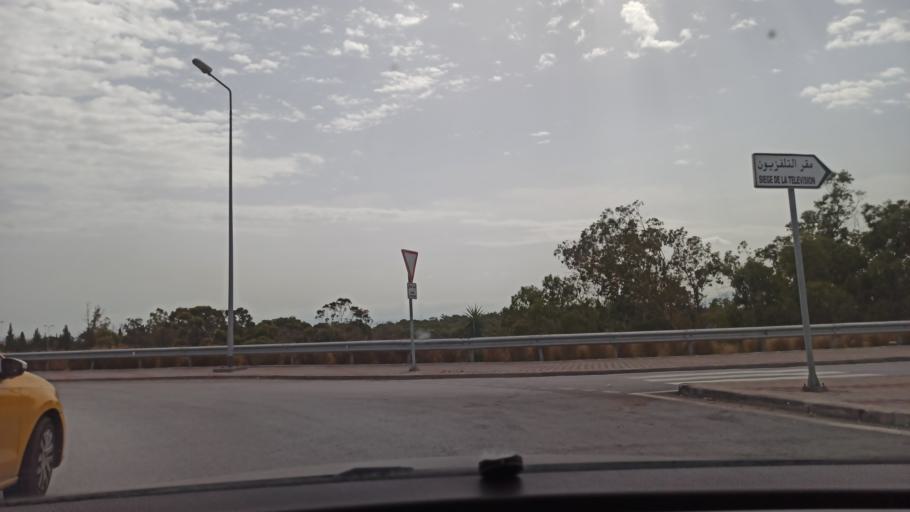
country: TN
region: Tunis
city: Tunis
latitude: 36.8294
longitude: 10.1612
